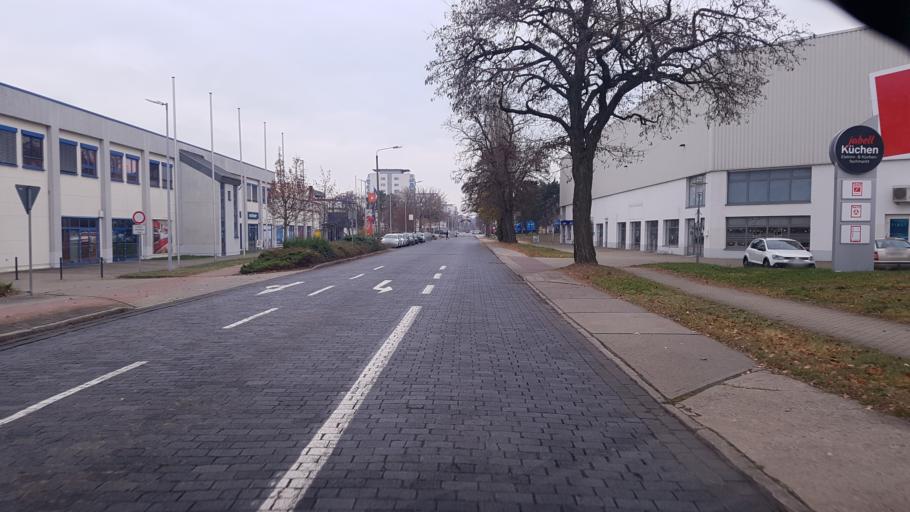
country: DE
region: Brandenburg
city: Eisenhuettenstadt
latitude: 52.1540
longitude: 14.6341
